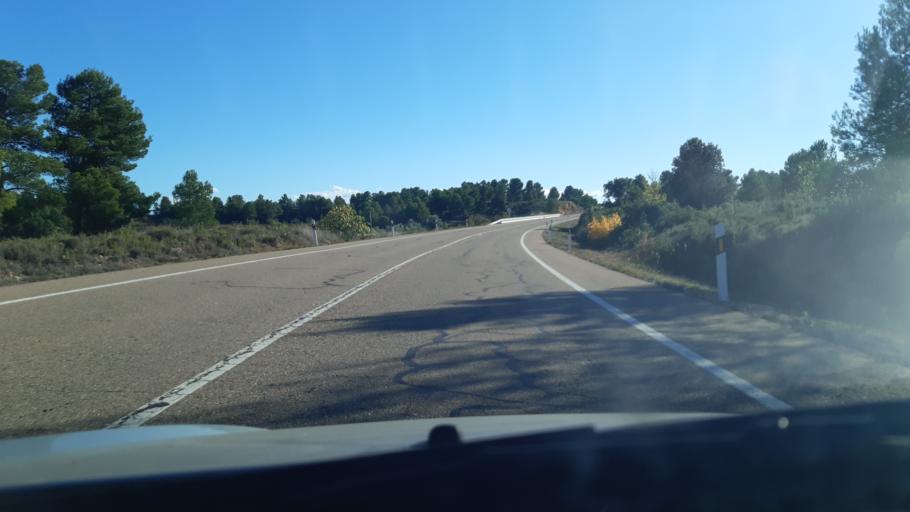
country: ES
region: Aragon
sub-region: Provincia de Teruel
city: Valjunquera
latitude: 40.9389
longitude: -0.0113
